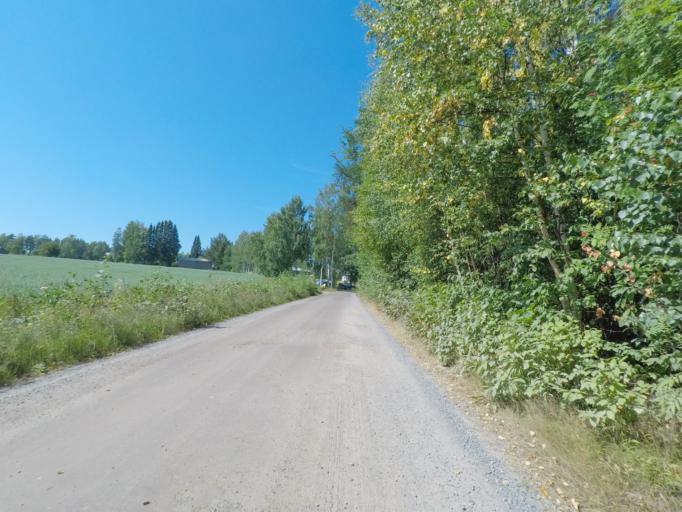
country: FI
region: Southern Savonia
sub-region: Mikkeli
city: Puumala
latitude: 61.4264
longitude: 28.0315
